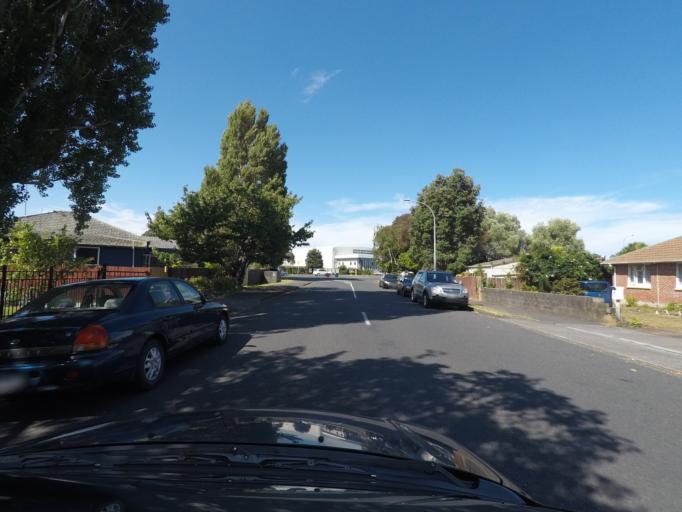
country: NZ
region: Auckland
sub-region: Auckland
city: Rosebank
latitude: -36.8847
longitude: 174.6821
